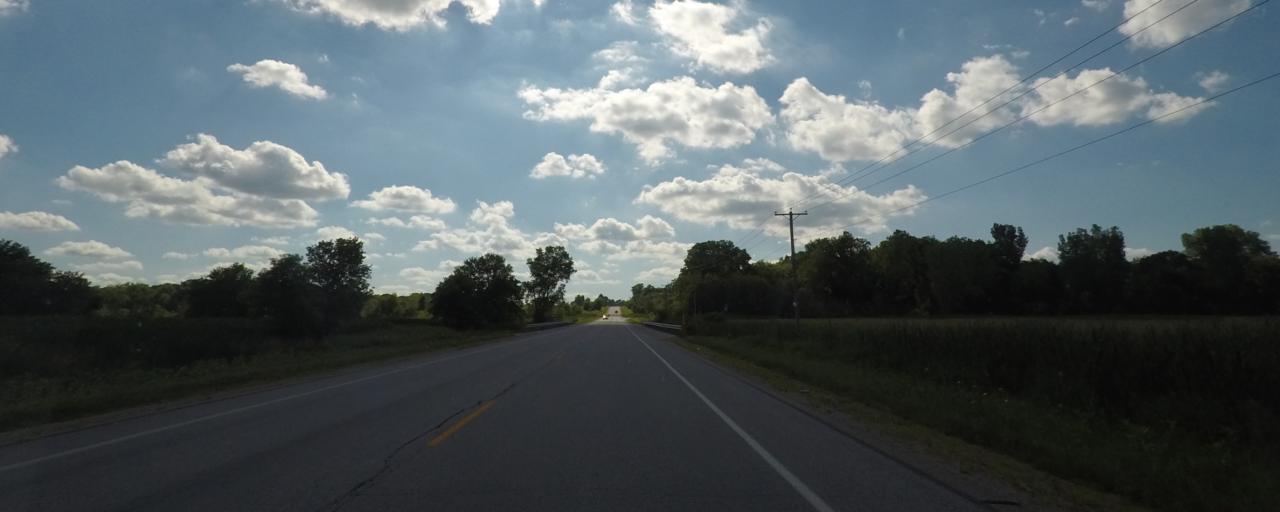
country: US
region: Wisconsin
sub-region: Rock County
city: Edgerton
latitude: 42.9198
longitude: -89.1177
